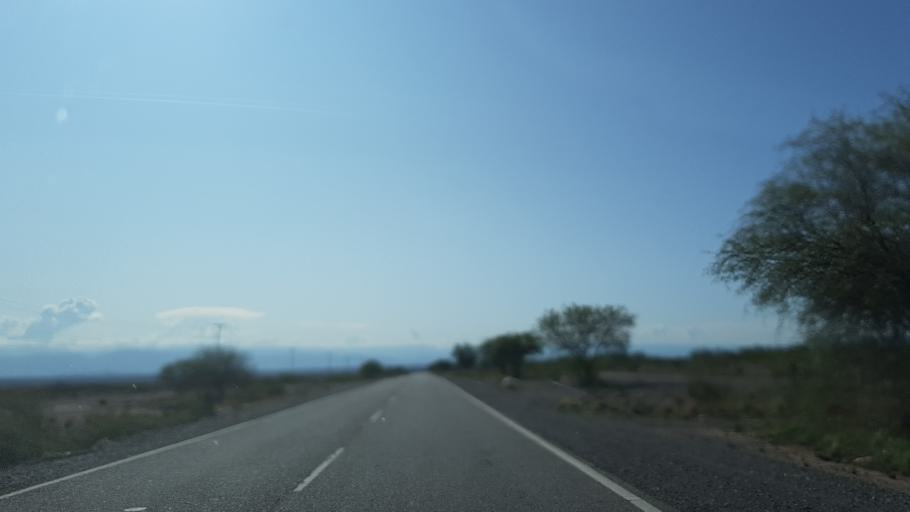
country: AR
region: San Juan
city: Caucete
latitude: -31.7537
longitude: -68.0854
